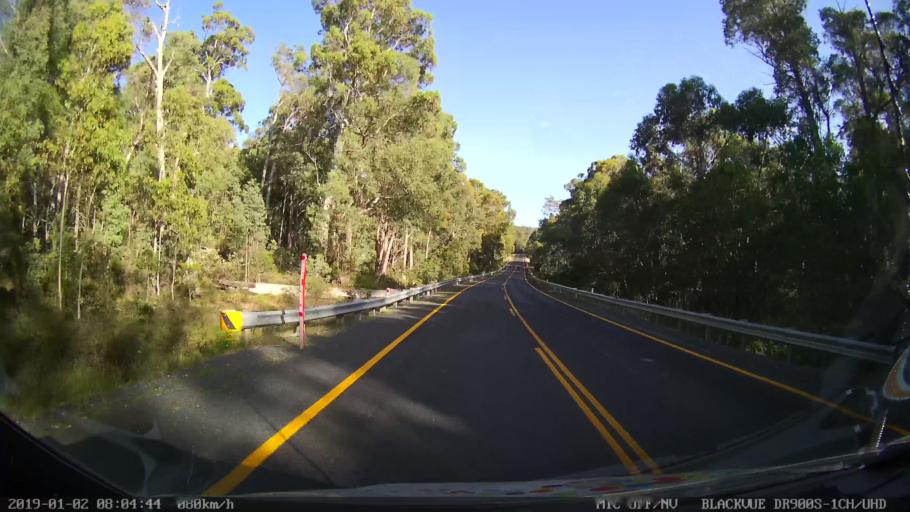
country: AU
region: New South Wales
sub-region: Tumut Shire
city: Tumut
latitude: -35.6593
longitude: 148.3921
